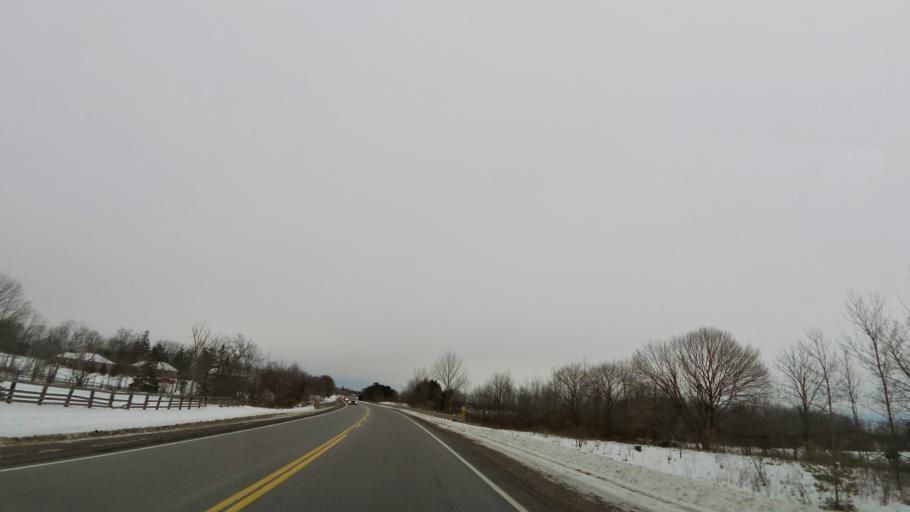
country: CA
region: Ontario
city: Ancaster
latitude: 43.2988
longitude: -80.1269
